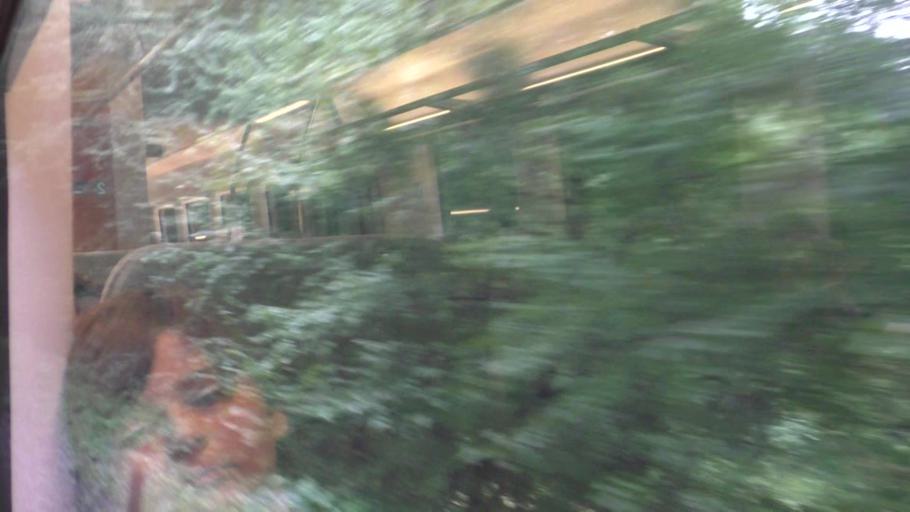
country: DE
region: Saxony
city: Neukirch/Lausitz
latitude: 51.0891
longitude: 14.2908
